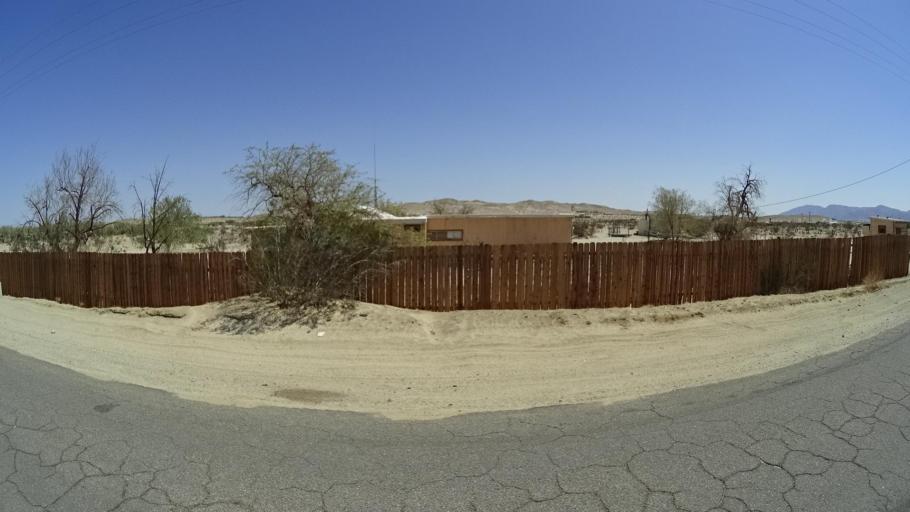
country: US
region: California
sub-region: Imperial County
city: Salton City
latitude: 33.1317
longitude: -116.1328
